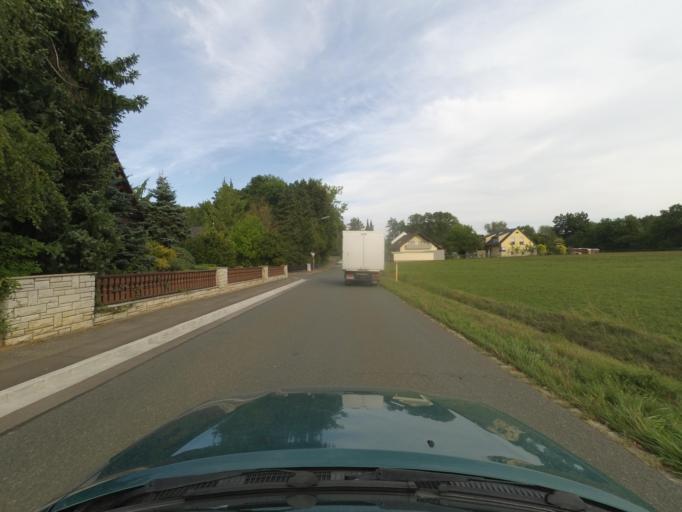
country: DE
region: Bavaria
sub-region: Regierungsbezirk Mittelfranken
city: Burgthann
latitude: 49.3256
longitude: 11.3156
